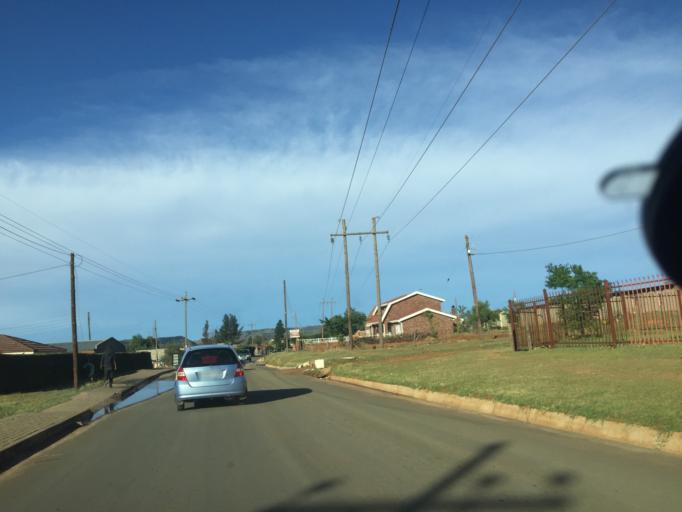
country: LS
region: Maseru
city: Maseru
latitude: -29.2906
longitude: 27.5294
